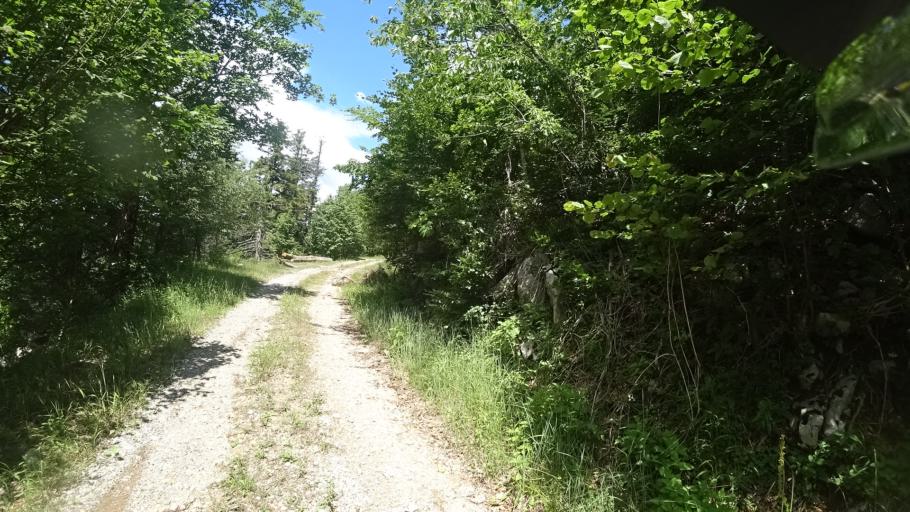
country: SI
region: Osilnica
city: Osilnica
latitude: 45.4800
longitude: 14.7105
